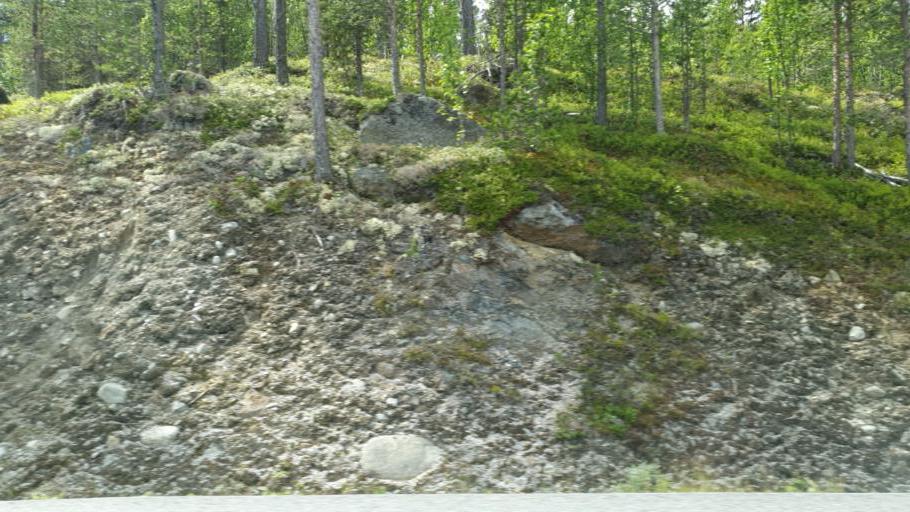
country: NO
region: Oppland
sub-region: Vaga
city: Vagamo
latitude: 61.7454
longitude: 9.0895
